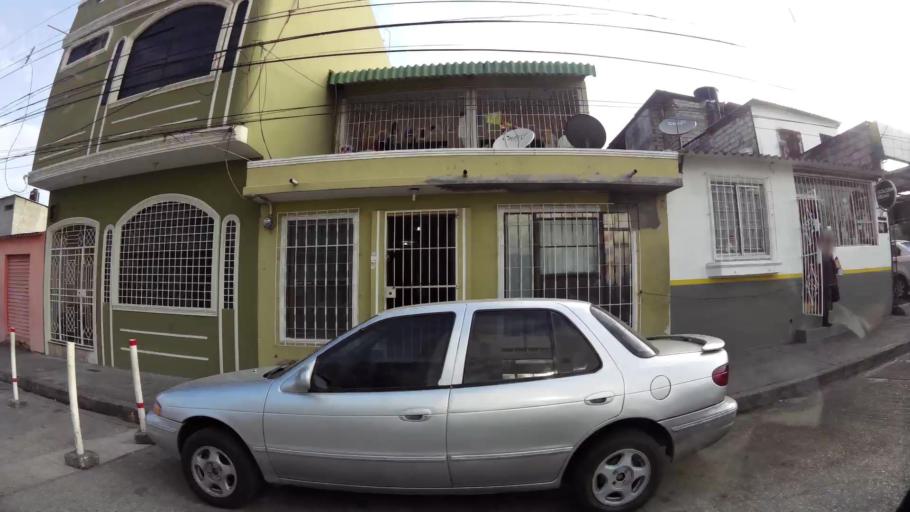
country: EC
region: Guayas
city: Eloy Alfaro
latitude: -2.1339
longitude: -79.8909
